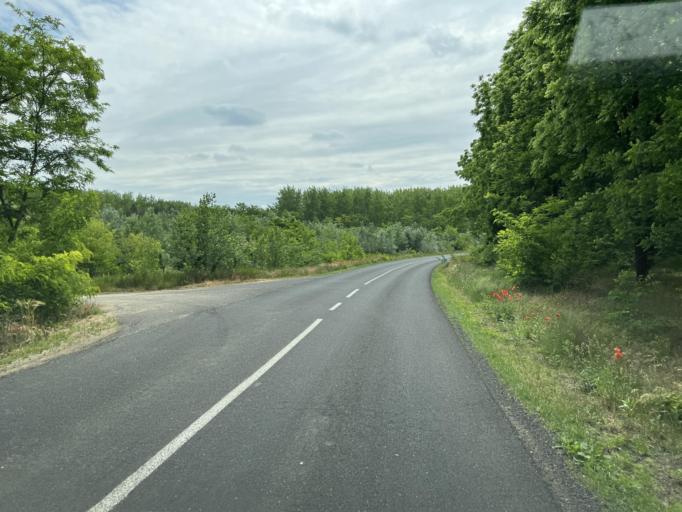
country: HU
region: Pest
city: Tapioszecso
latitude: 47.4755
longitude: 19.6154
